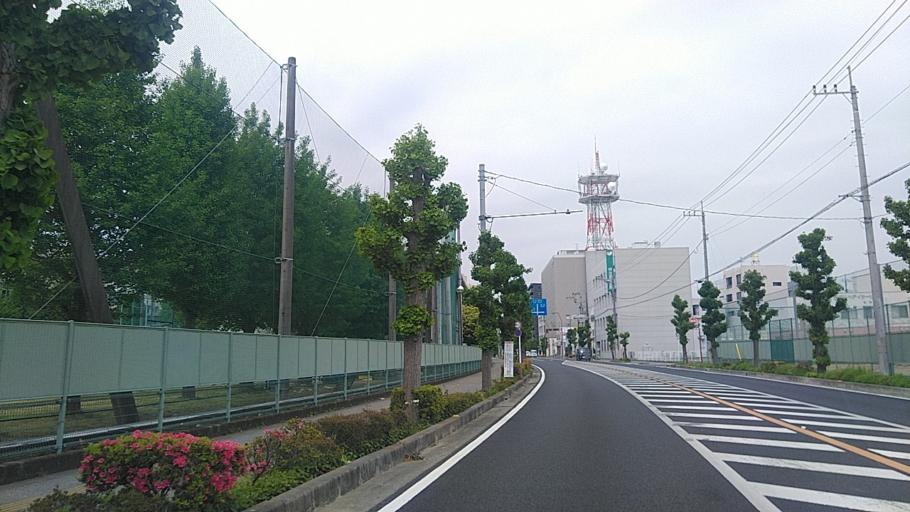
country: JP
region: Saitama
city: Kumagaya
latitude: 36.1451
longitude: 139.3934
